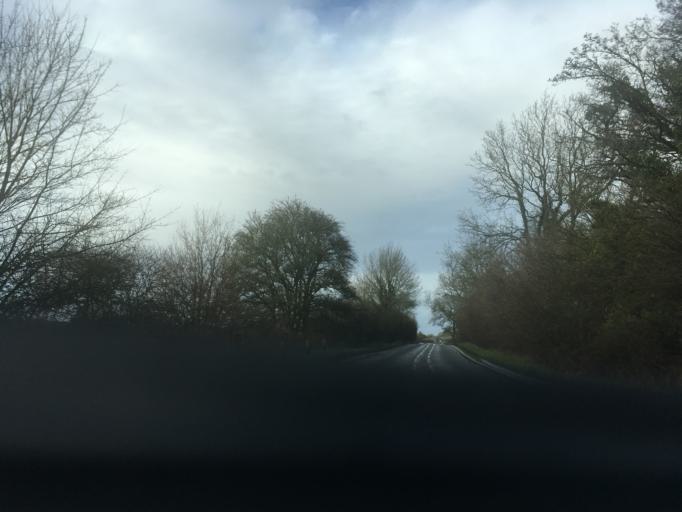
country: GB
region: England
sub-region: Oxfordshire
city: Eynsham
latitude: 51.7655
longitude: -1.3579
